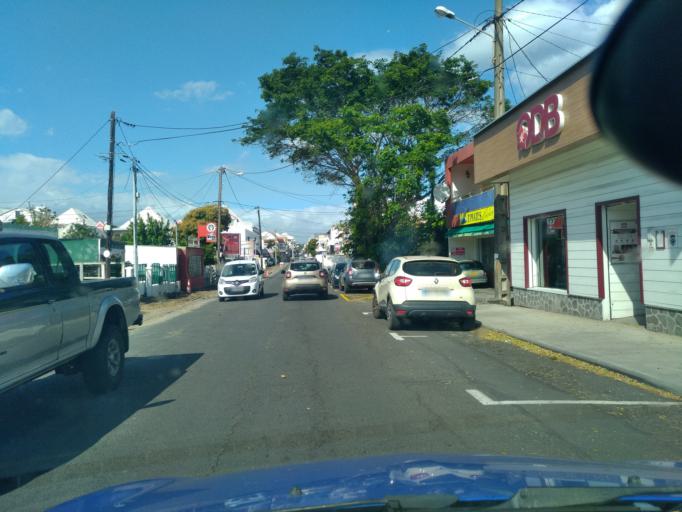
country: RE
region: Reunion
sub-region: Reunion
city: Saint-Pierre
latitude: -21.3360
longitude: 55.4689
